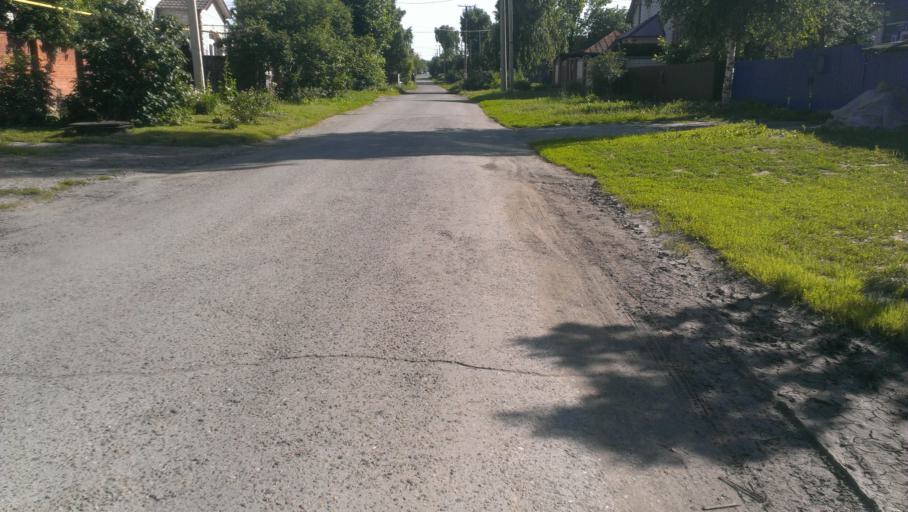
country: RU
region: Altai Krai
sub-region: Gorod Barnaulskiy
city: Barnaul
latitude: 53.3572
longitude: 83.7412
